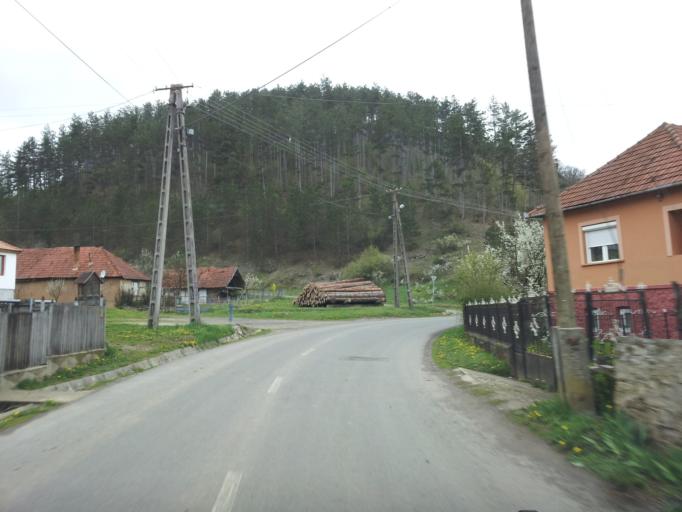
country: HU
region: Borsod-Abauj-Zemplen
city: Rudabanya
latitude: 48.4860
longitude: 20.6262
